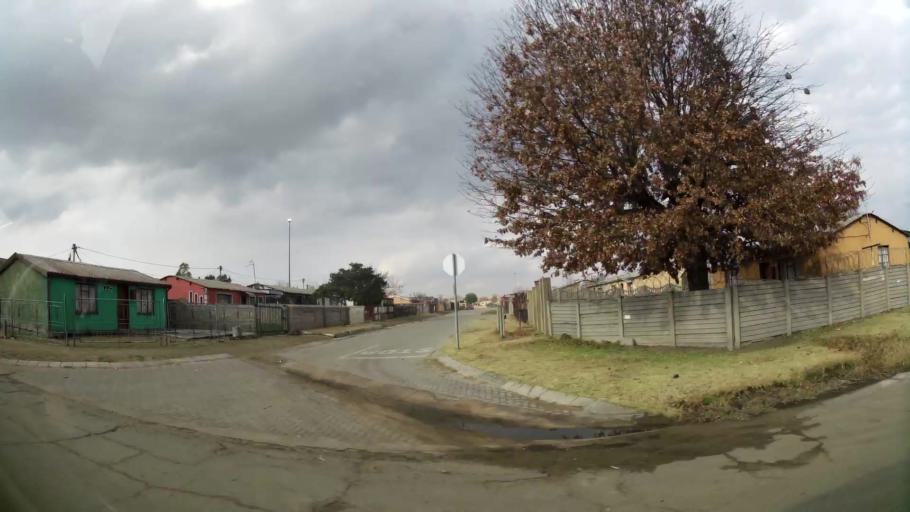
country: ZA
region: Orange Free State
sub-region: Fezile Dabi District Municipality
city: Sasolburg
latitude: -26.8418
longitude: 27.8401
